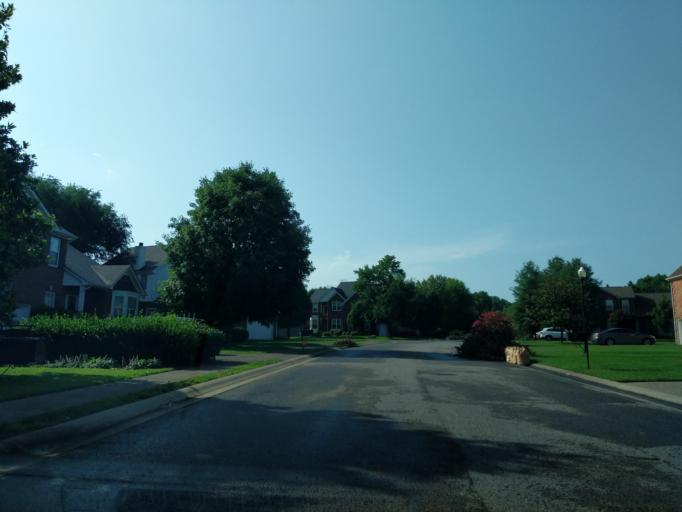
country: US
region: Tennessee
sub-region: Cheatham County
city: Pegram
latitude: 36.0341
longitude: -86.9606
